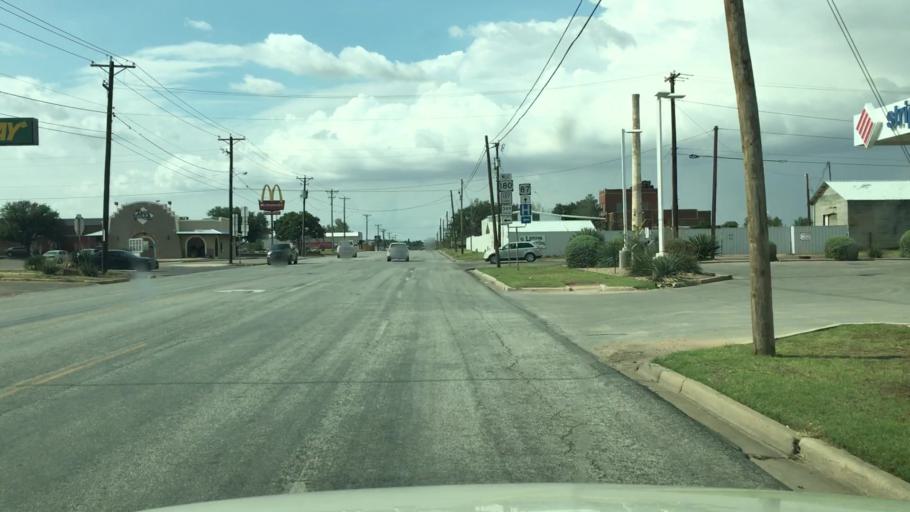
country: US
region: Texas
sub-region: Dawson County
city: Lamesa
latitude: 32.7364
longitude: -101.9500
